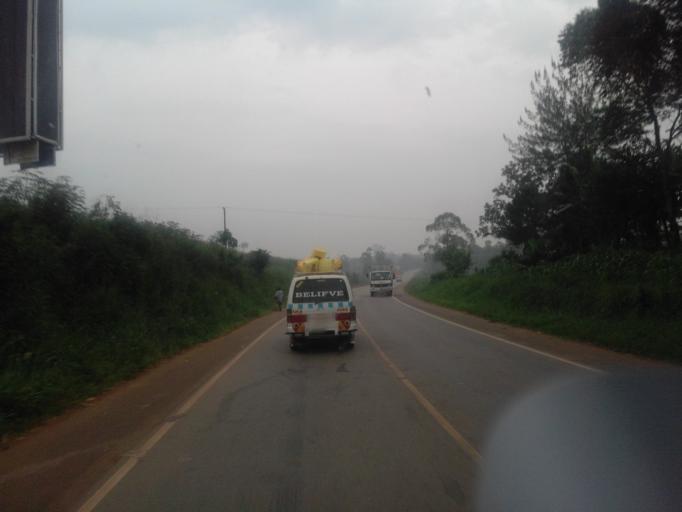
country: UG
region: Central Region
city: Lugazi
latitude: 0.3756
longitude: 32.9117
